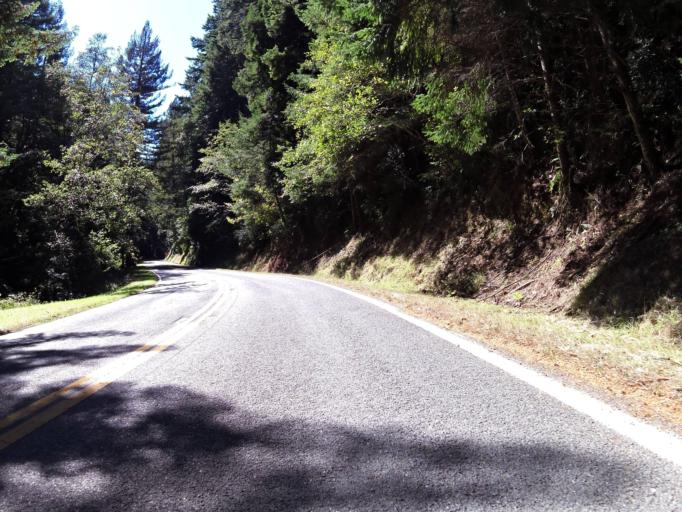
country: US
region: California
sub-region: Humboldt County
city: Redway
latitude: 39.7895
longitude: -123.8171
